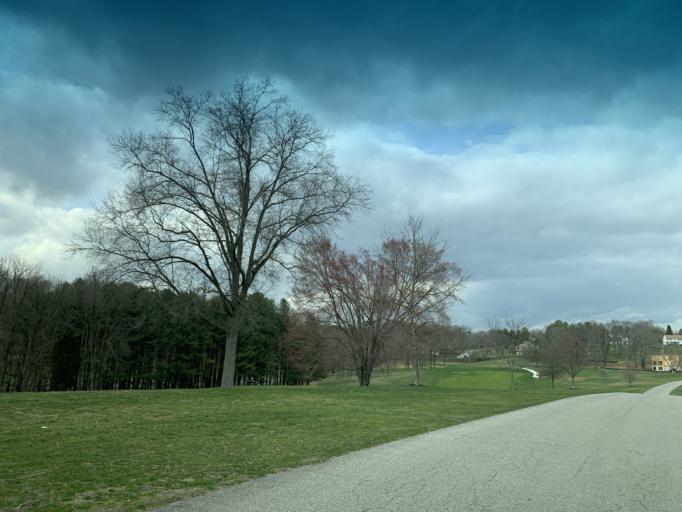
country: US
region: Maryland
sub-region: Harford County
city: North Bel Air
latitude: 39.5260
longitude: -76.3802
